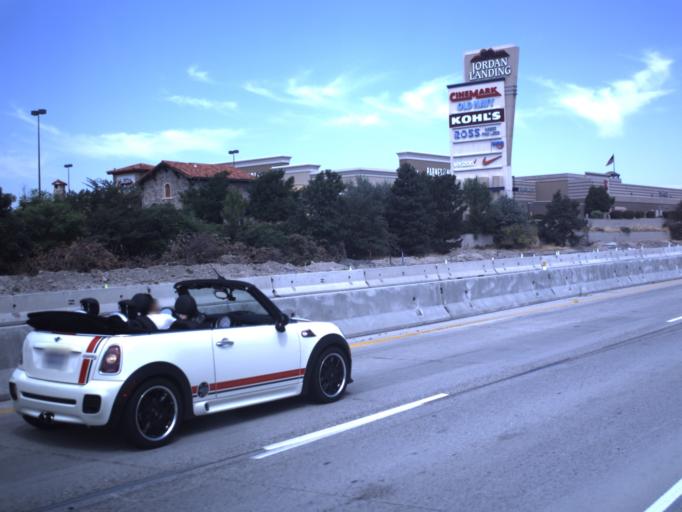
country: US
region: Utah
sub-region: Salt Lake County
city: West Jordan
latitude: 40.6199
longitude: -111.9763
